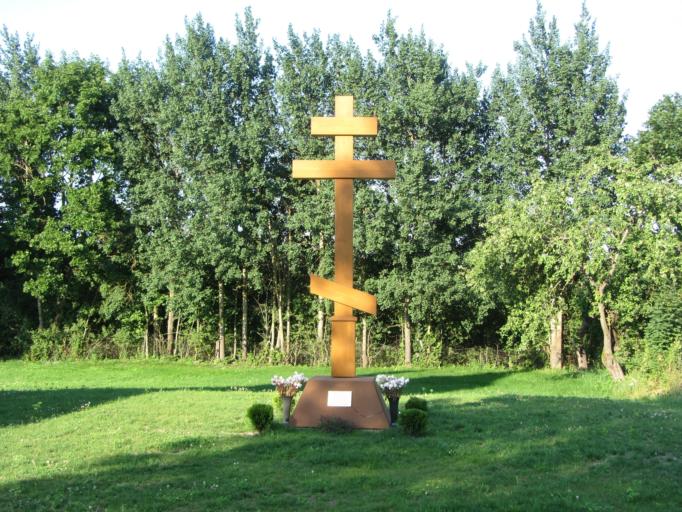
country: LT
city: Salcininkai
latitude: 54.4186
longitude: 25.3215
